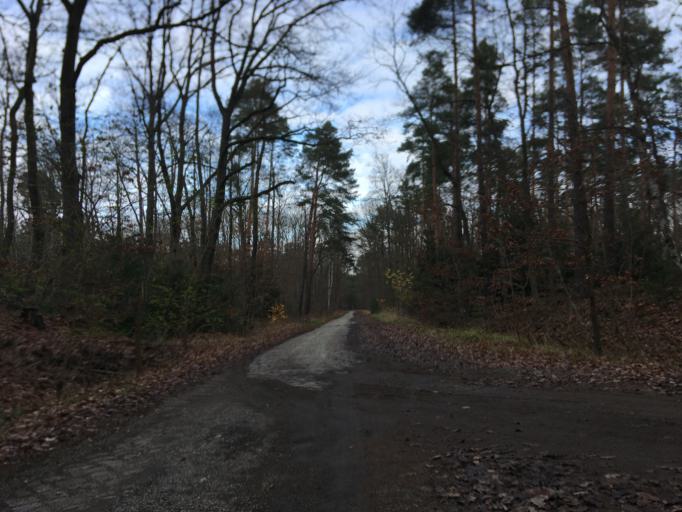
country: DE
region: Brandenburg
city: Tauer
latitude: 51.9428
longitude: 14.5146
